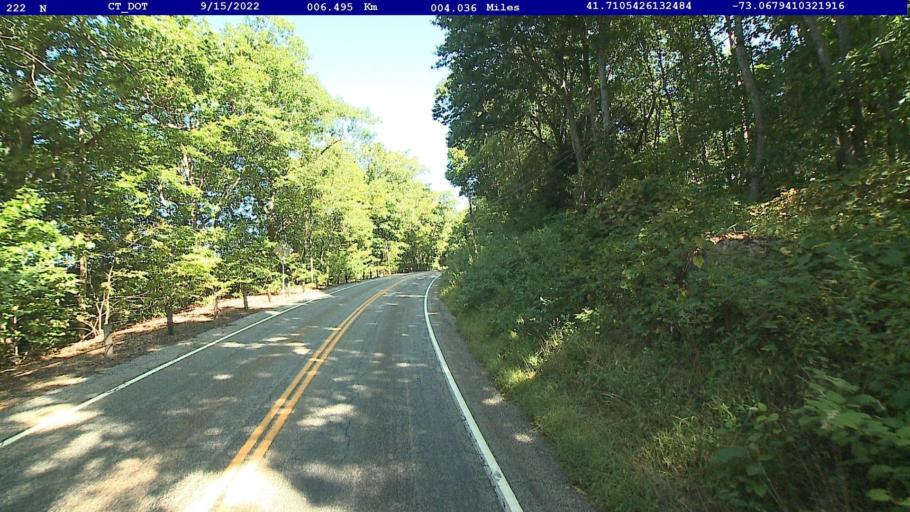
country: US
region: Connecticut
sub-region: Litchfield County
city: Thomaston
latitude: 41.7106
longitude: -73.0679
